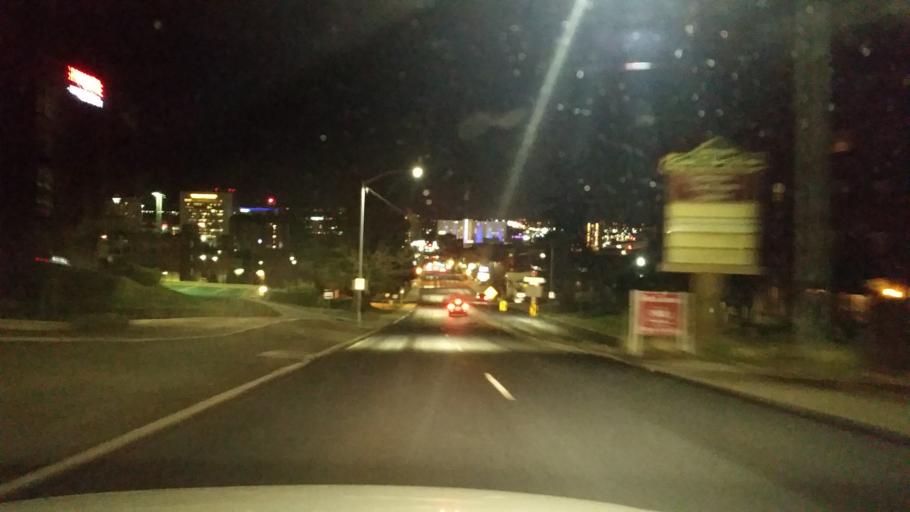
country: US
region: Washington
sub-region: Spokane County
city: Spokane
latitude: 47.6481
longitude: -117.4180
